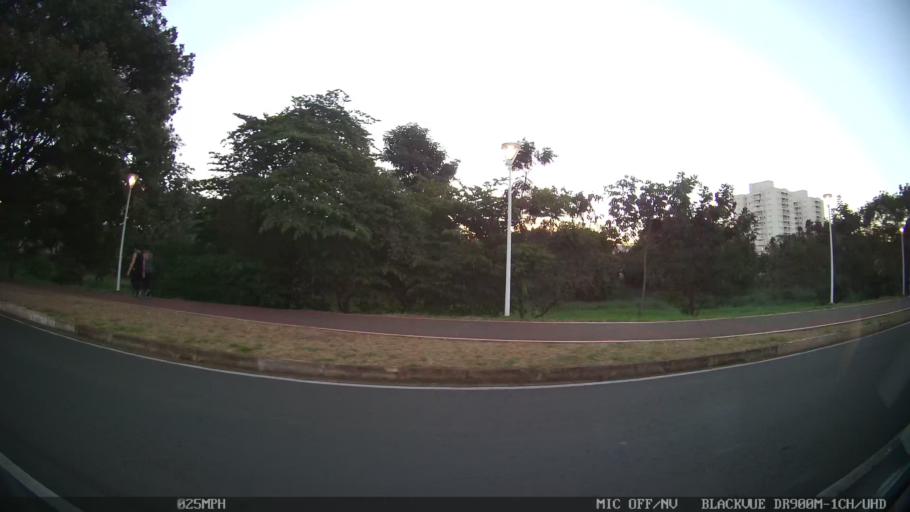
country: BR
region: Sao Paulo
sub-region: Sao Jose Do Rio Preto
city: Sao Jose do Rio Preto
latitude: -20.8407
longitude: -49.3939
